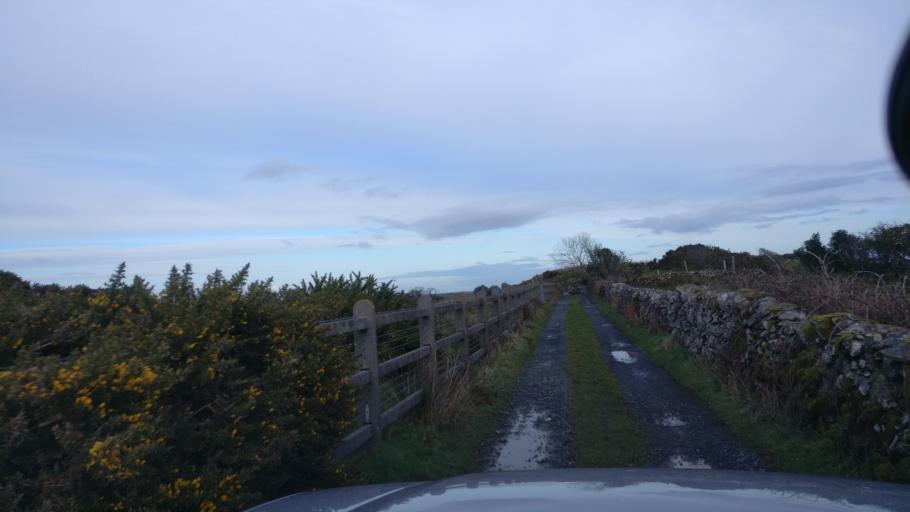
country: IE
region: Connaught
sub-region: County Galway
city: Oughterard
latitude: 53.5247
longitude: -9.3800
